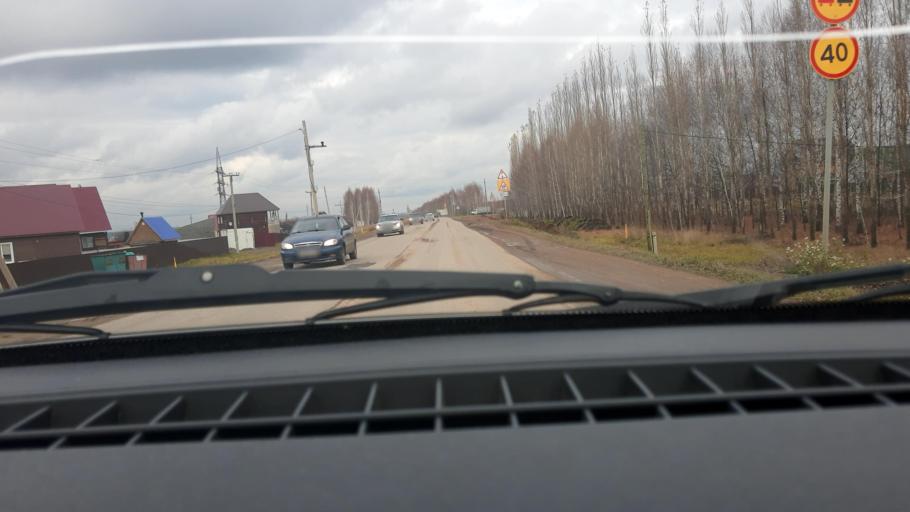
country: RU
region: Bashkortostan
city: Iglino
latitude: 54.8190
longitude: 56.4193
